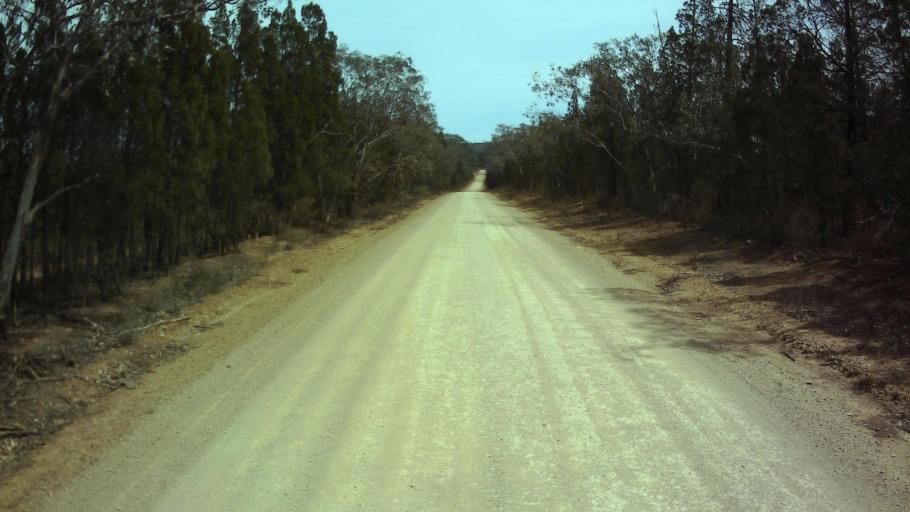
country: AU
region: New South Wales
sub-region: Weddin
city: Grenfell
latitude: -33.9108
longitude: 148.4121
